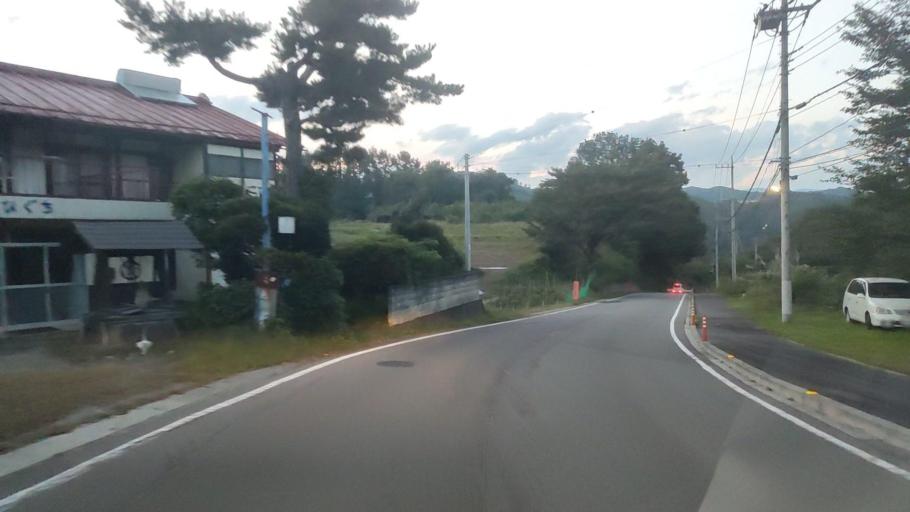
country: JP
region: Gunma
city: Nakanojomachi
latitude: 36.5432
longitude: 138.6021
